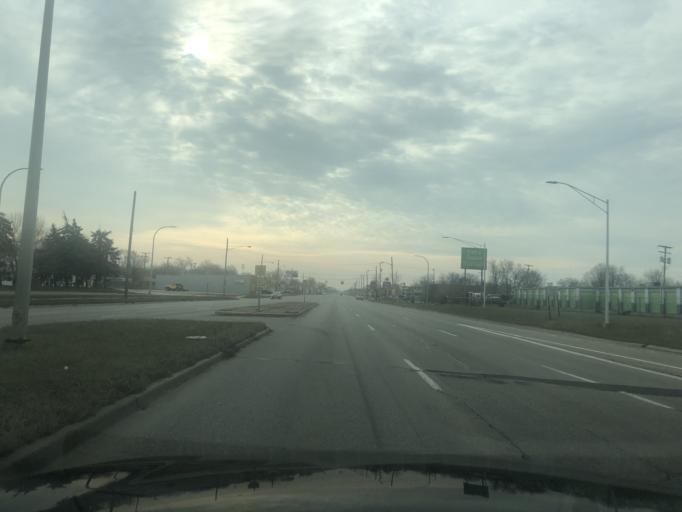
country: US
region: Michigan
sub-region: Wayne County
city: Lincoln Park
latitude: 42.2412
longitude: -83.1951
